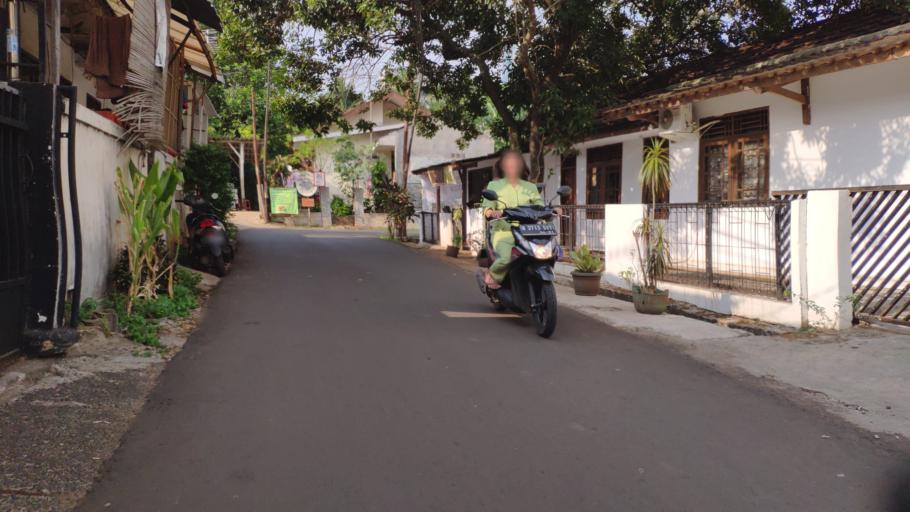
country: ID
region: West Java
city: Pamulang
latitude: -6.2963
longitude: 106.8018
